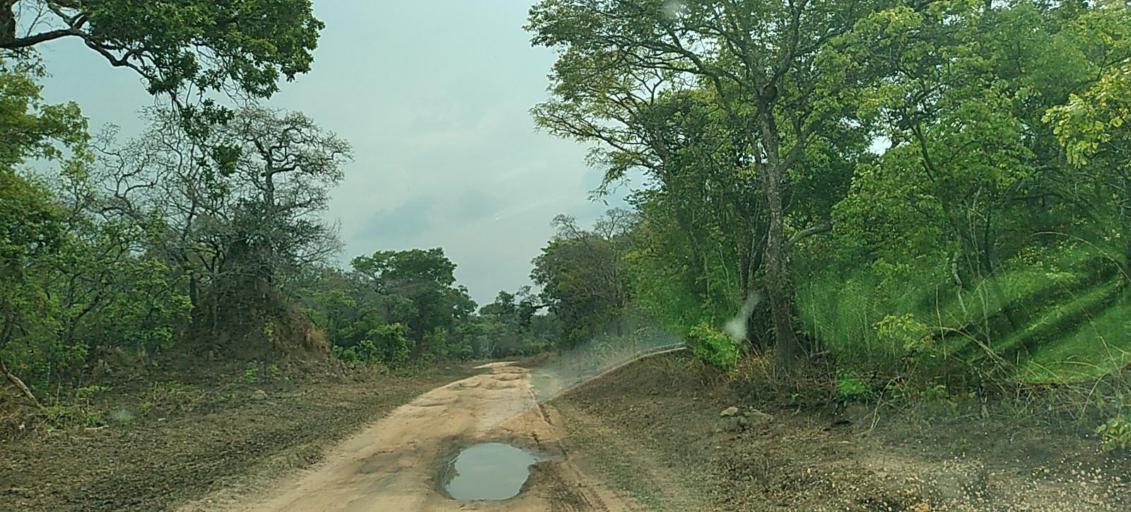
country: ZM
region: North-Western
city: Mwinilunga
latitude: -11.4689
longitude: 24.4662
